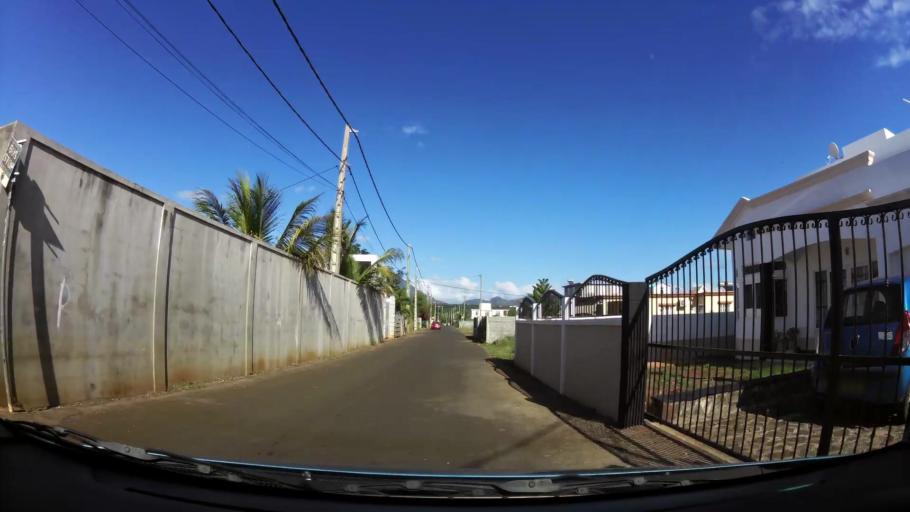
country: MU
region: Black River
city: Albion
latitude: -20.2023
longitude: 57.4112
